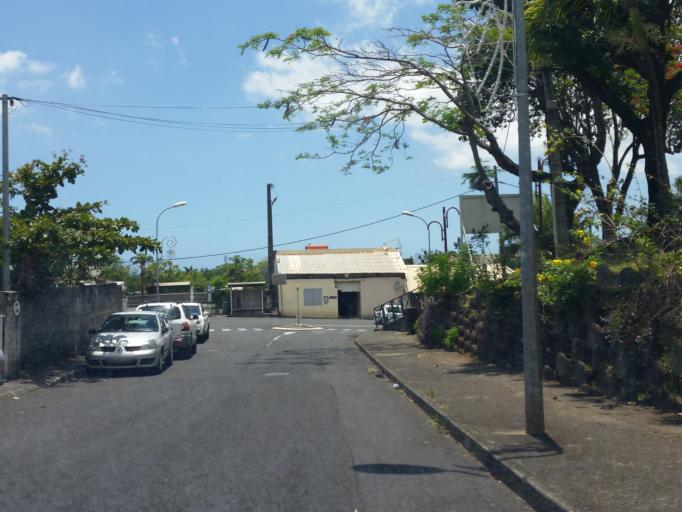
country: RE
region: Reunion
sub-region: Reunion
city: Sainte-Marie
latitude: -20.9151
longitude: 55.5074
